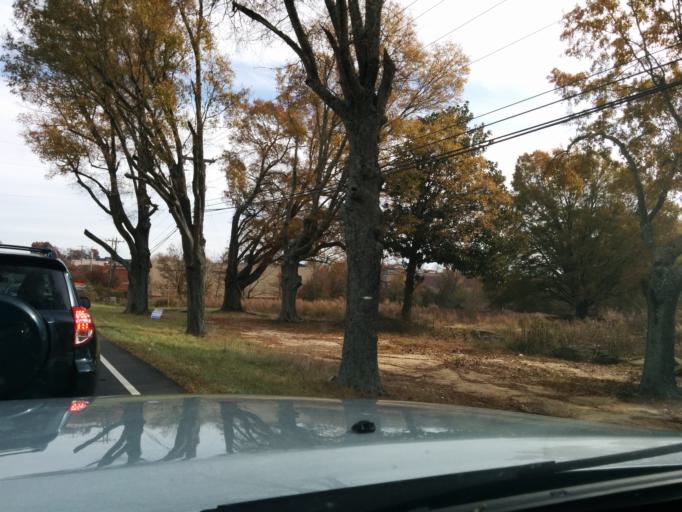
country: US
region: North Carolina
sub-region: Iredell County
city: Mooresville
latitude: 35.5964
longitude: -80.8798
